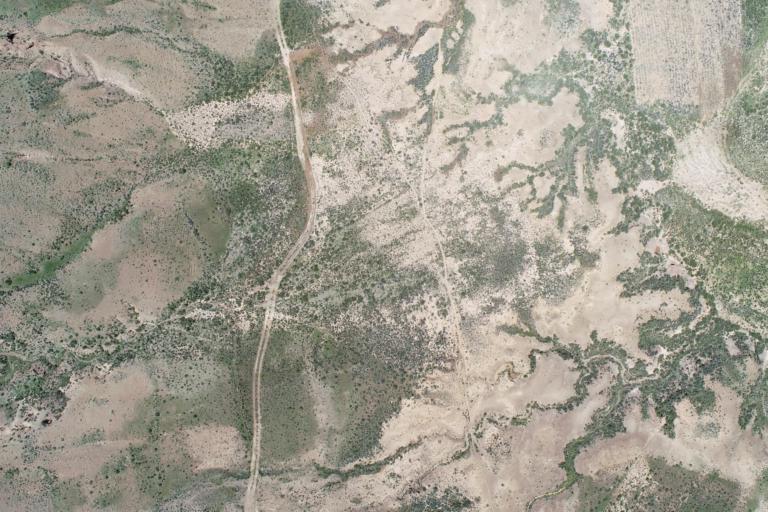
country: BO
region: La Paz
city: Curahuara de Carangas
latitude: -17.3189
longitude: -68.5059
